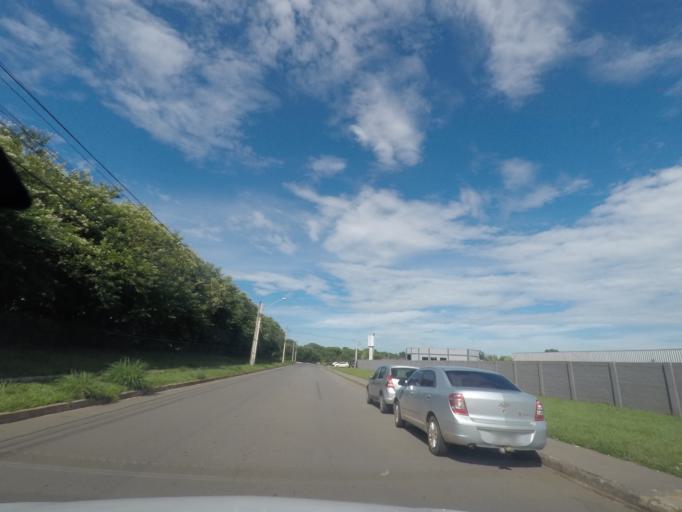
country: BR
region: Goias
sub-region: Aparecida De Goiania
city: Aparecida de Goiania
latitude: -16.7920
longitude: -49.2611
